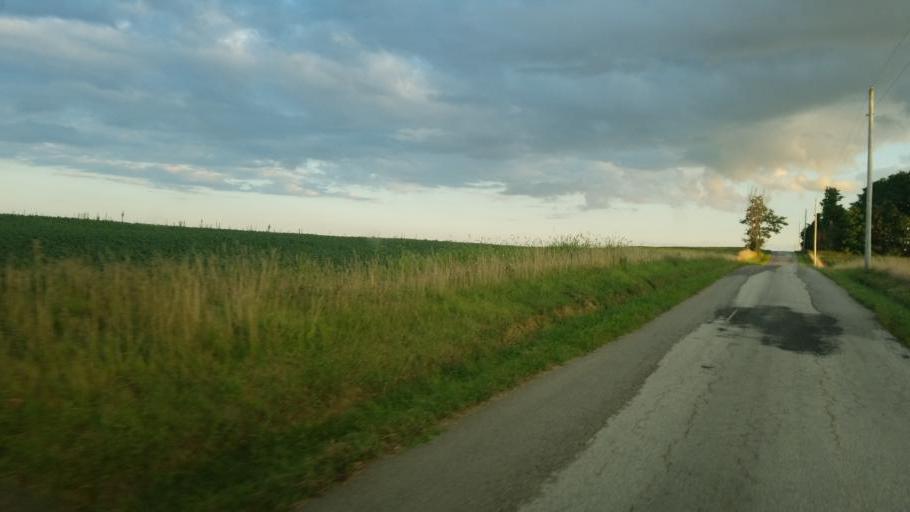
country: US
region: Ohio
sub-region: Richland County
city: Mansfield
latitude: 40.8284
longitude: -82.5424
